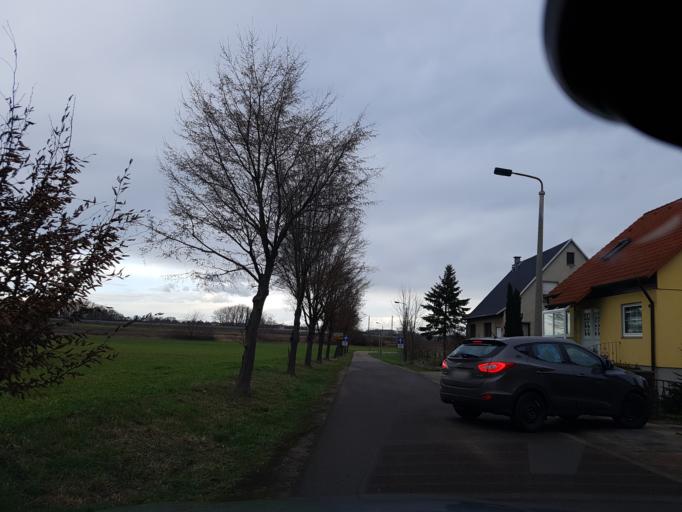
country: DE
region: Saxony
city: Stauchitz
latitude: 51.2670
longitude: 13.2388
